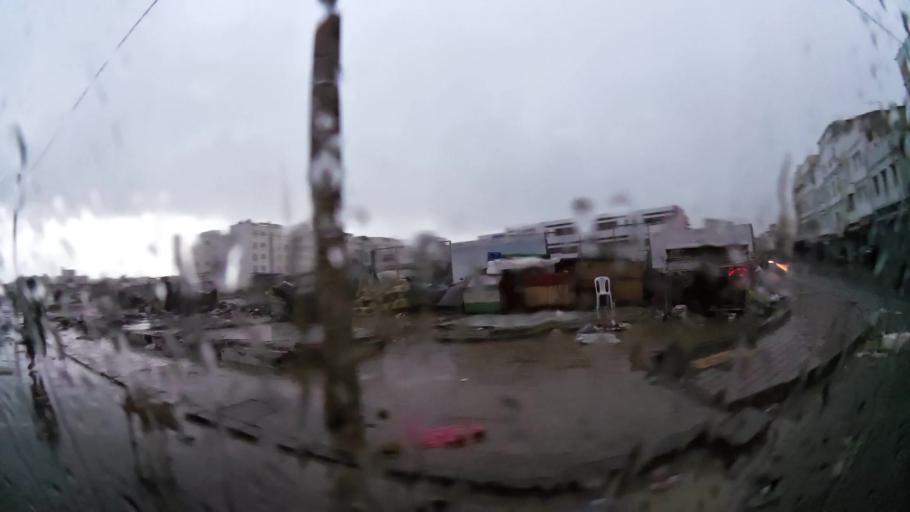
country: MA
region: Grand Casablanca
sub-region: Casablanca
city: Casablanca
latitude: 33.5659
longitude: -7.5987
